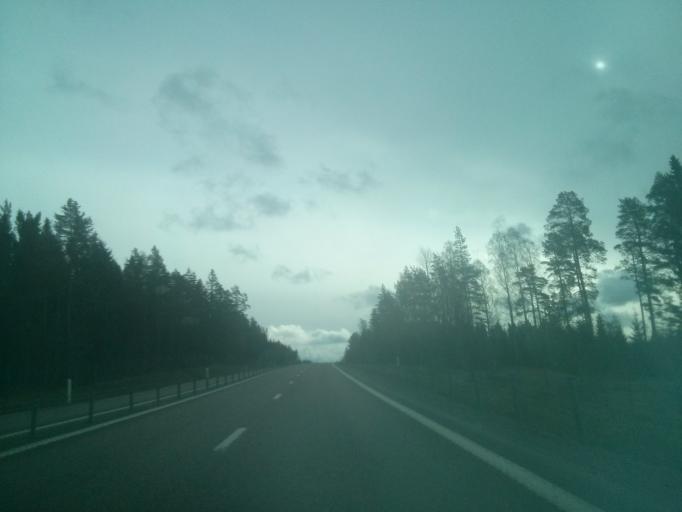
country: SE
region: Vaesternorrland
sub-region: Timra Kommun
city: Soraker
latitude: 62.5451
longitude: 17.5856
